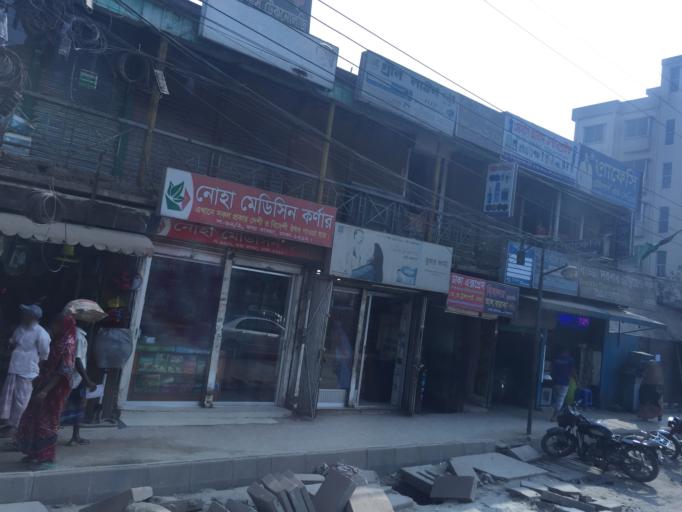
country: BD
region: Dhaka
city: Paltan
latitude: 23.7778
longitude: 90.4259
